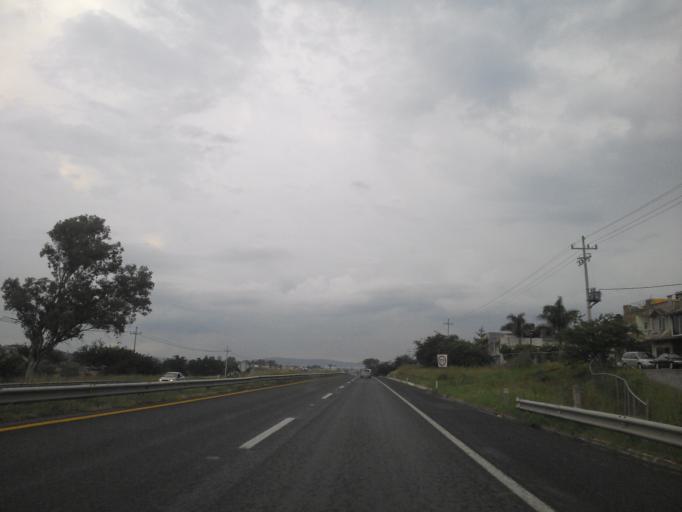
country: MX
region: Jalisco
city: Zapotlanejo
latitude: 20.6187
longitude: -103.0606
